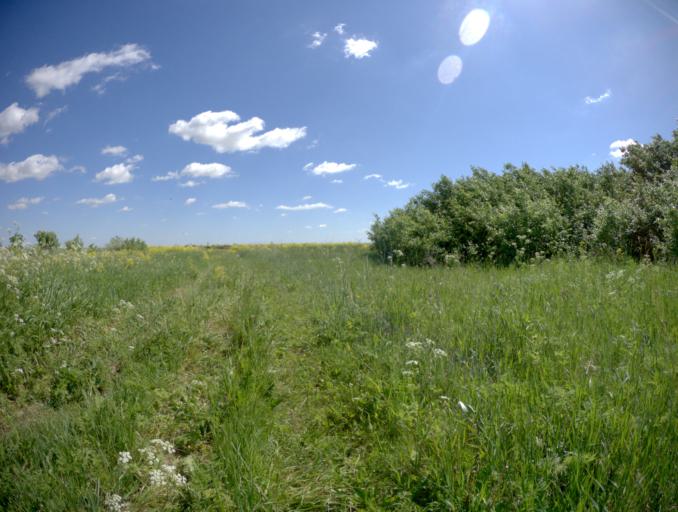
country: RU
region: Ivanovo
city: Gavrilov Posad
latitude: 56.4883
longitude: 40.2448
